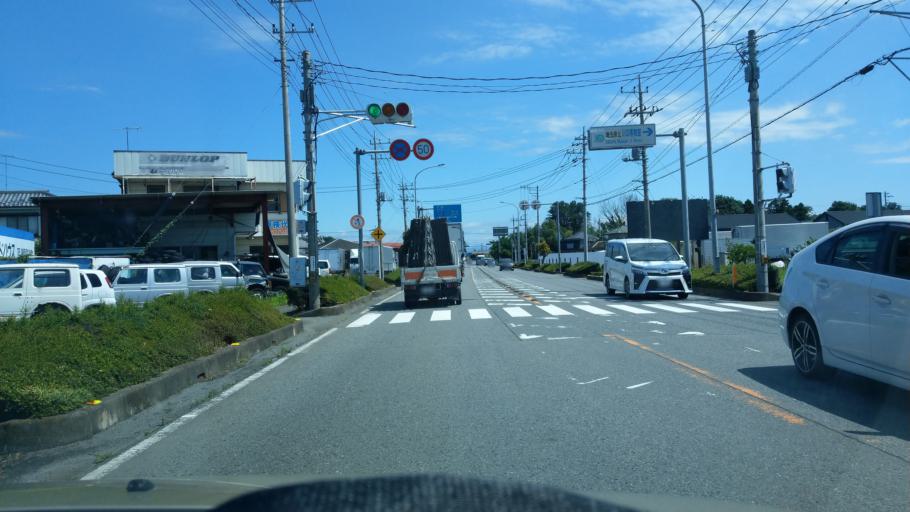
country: JP
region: Saitama
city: Yorii
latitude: 36.1174
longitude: 139.2108
